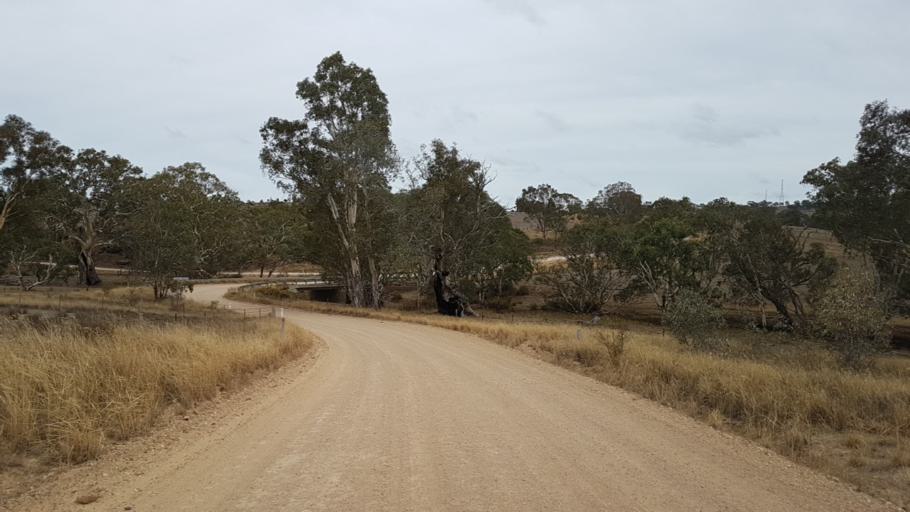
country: AU
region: South Australia
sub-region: Adelaide Hills
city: Birdwood
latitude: -34.8784
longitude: 139.0838
